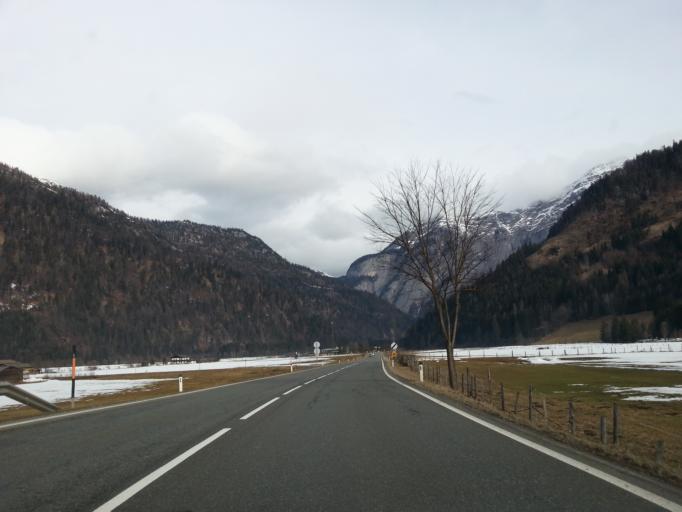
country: AT
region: Salzburg
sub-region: Politischer Bezirk Zell am See
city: Saalfelden am Steinernen Meer
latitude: 47.4557
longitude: 12.8304
